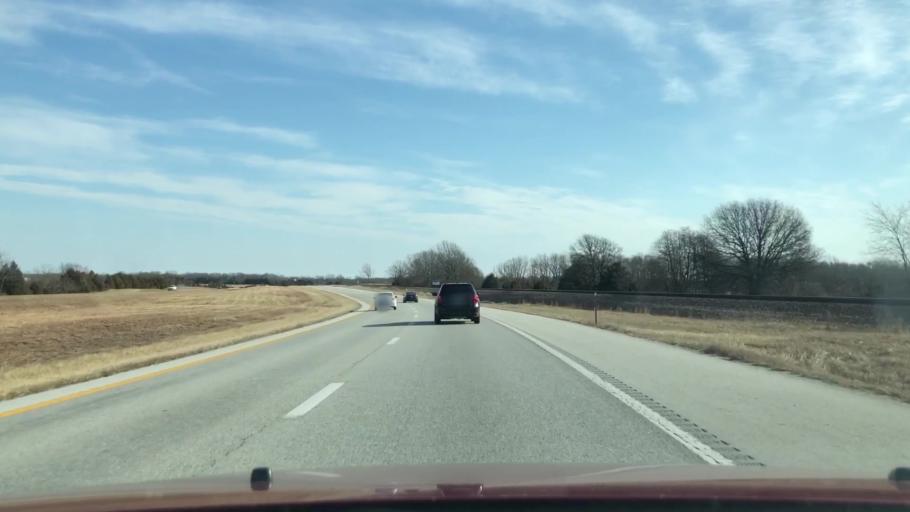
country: US
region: Missouri
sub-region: Webster County
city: Seymour
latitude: 37.1293
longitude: -92.7336
